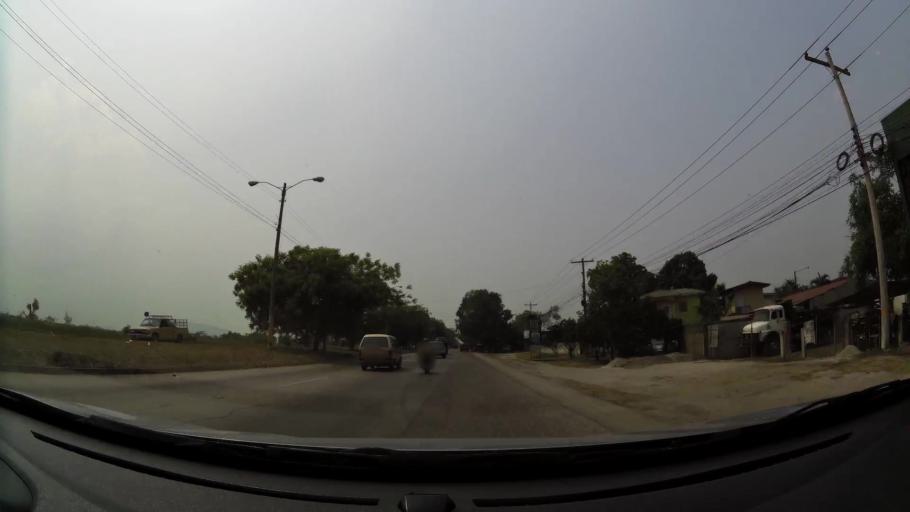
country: HN
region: Cortes
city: La Lima
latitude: 15.4355
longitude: -87.9367
